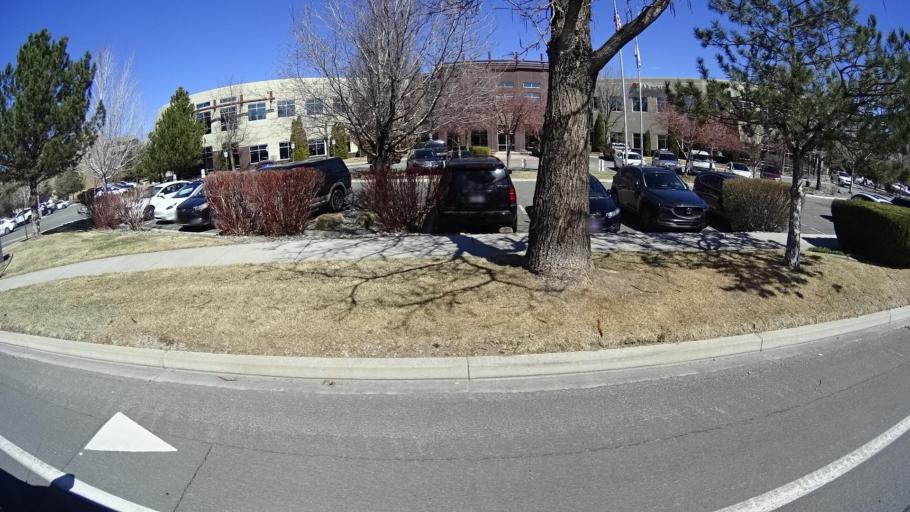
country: US
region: Nevada
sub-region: Washoe County
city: Reno
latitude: 39.4656
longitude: -119.7785
